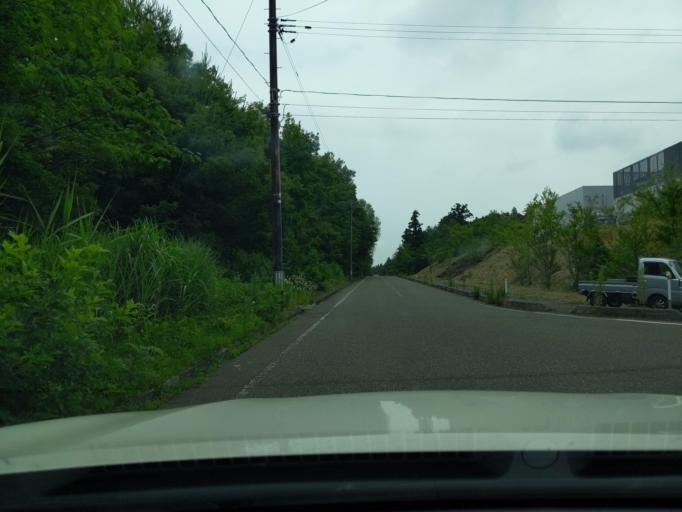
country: JP
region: Niigata
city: Kashiwazaki
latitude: 37.3390
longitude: 138.5840
